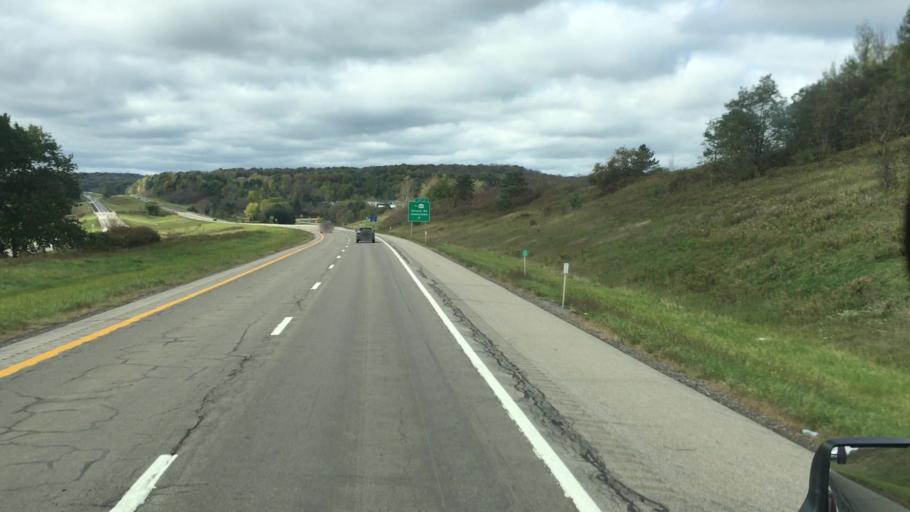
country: US
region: New York
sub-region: Chautauqua County
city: Celoron
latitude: 42.1237
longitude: -79.2658
